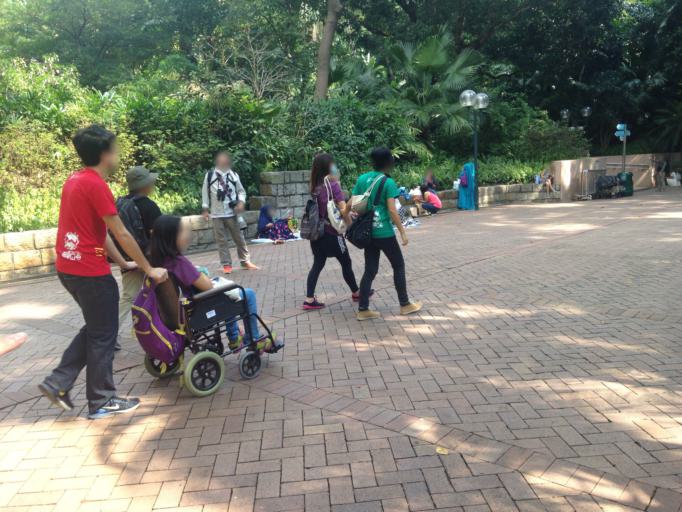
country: HK
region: Wanchai
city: Wan Chai
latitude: 22.2984
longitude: 114.1707
